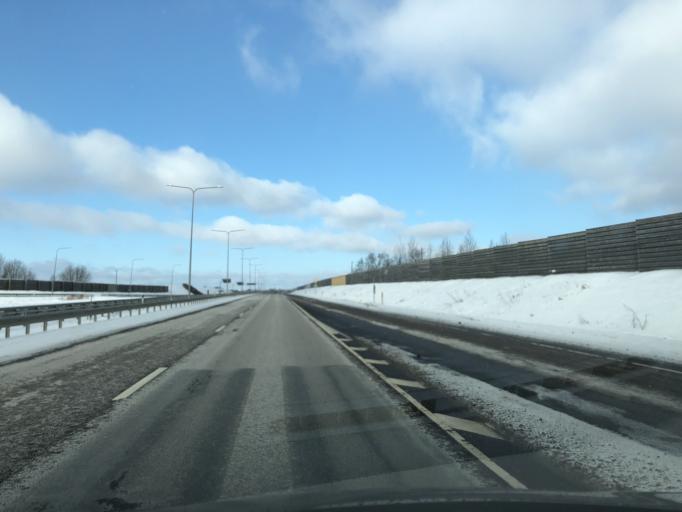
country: EE
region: Jaervamaa
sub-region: Paide linn
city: Paide
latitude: 58.9187
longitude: 25.6191
